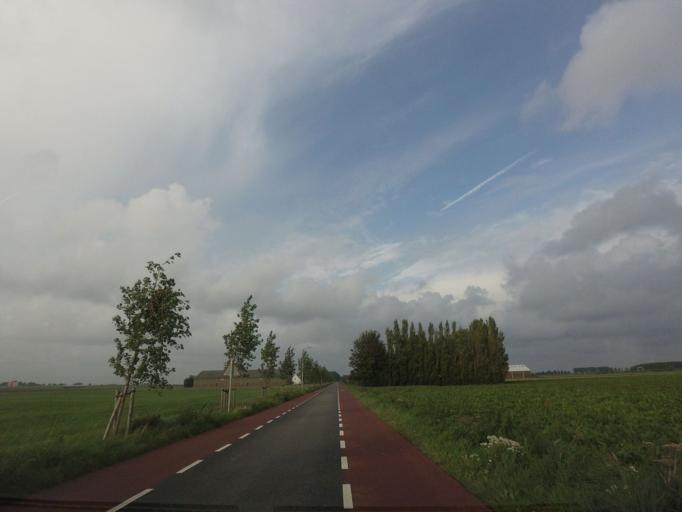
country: NL
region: South Holland
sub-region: Gemeente Kaag en Braassem
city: Oude Wetering
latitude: 52.2366
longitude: 4.6339
